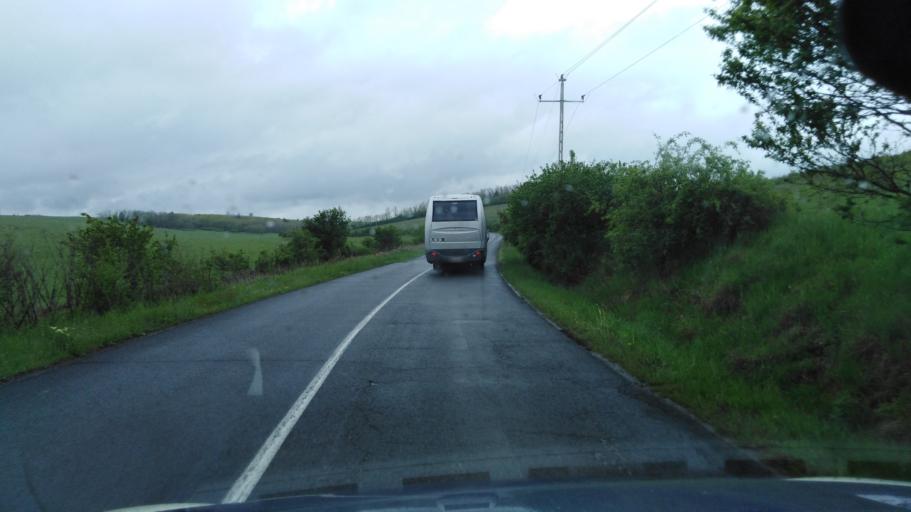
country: HU
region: Nograd
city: Rimoc
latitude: 48.0078
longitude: 19.6079
